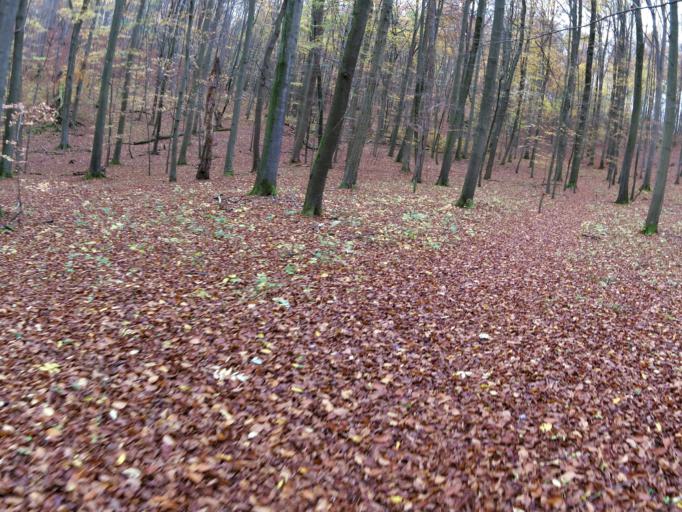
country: DE
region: Thuringia
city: Bischofroda
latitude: 51.0786
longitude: 10.3793
